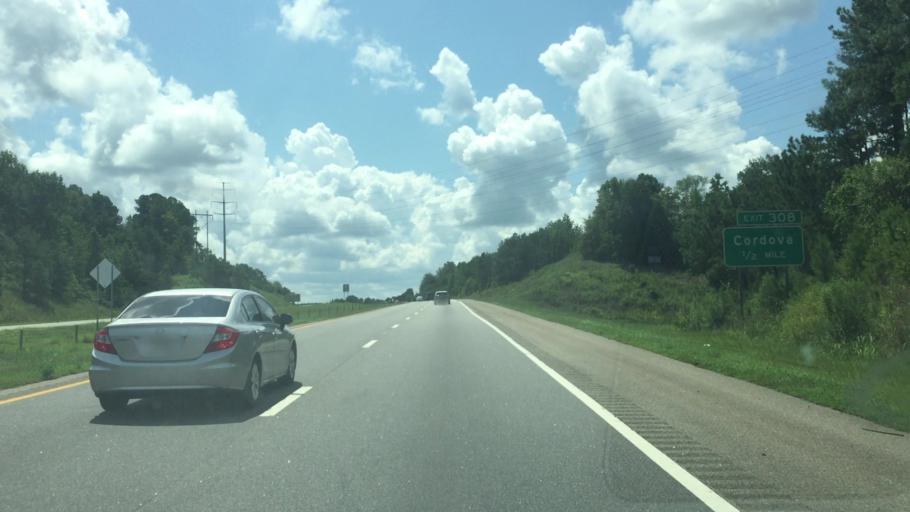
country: US
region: North Carolina
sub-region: Richmond County
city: Cordova
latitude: 34.9397
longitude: -79.8425
